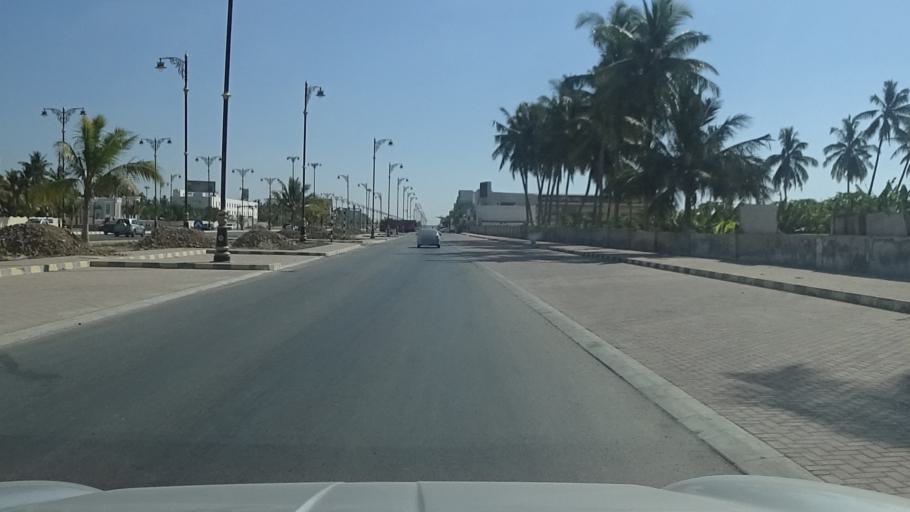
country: OM
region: Zufar
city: Salalah
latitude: 17.0360
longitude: 54.1580
